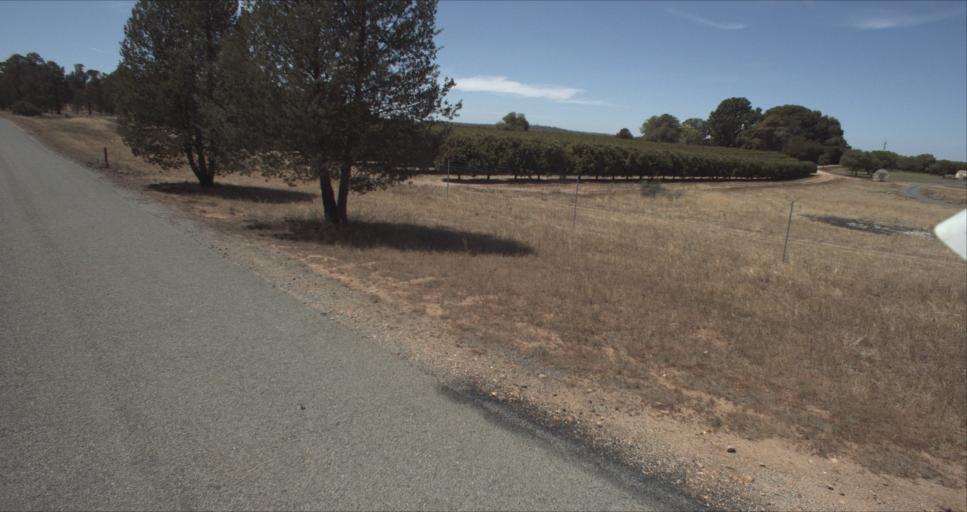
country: AU
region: New South Wales
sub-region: Leeton
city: Leeton
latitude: -34.6744
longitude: 146.4436
